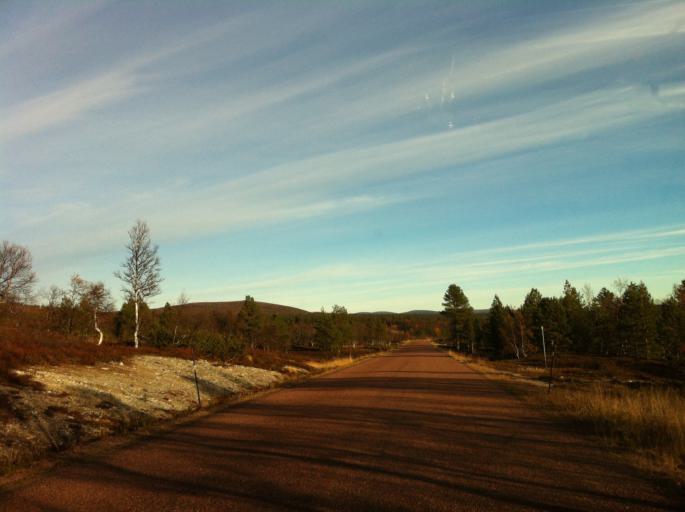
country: NO
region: Hedmark
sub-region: Engerdal
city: Engerdal
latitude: 62.0833
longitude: 12.1024
